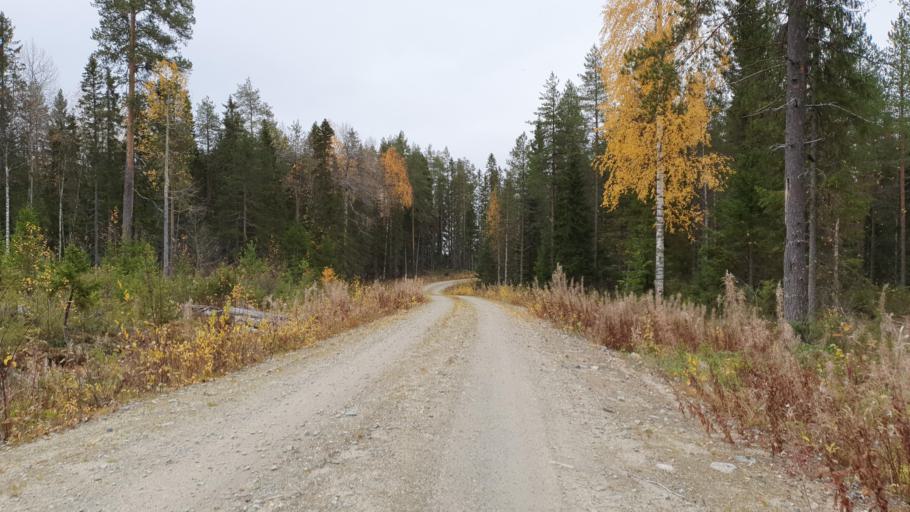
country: FI
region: Kainuu
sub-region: Kehys-Kainuu
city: Kuhmo
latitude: 64.4447
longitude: 29.6406
